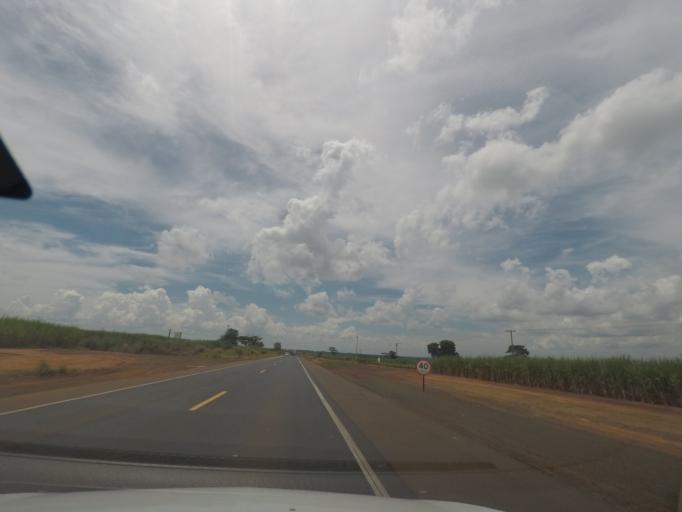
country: BR
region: Sao Paulo
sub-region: Barretos
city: Barretos
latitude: -20.3869
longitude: -48.6408
